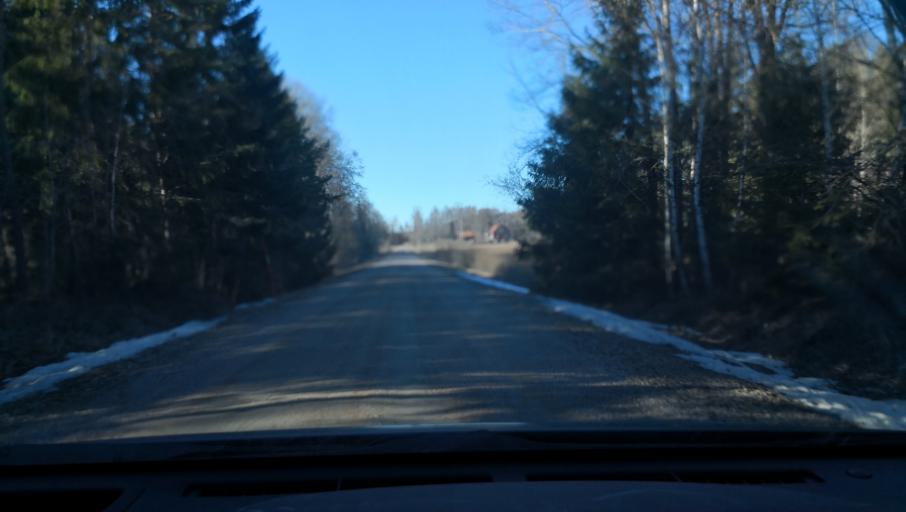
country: SE
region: Vaestmanland
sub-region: Sala Kommun
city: Sala
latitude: 60.1680
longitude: 16.6352
